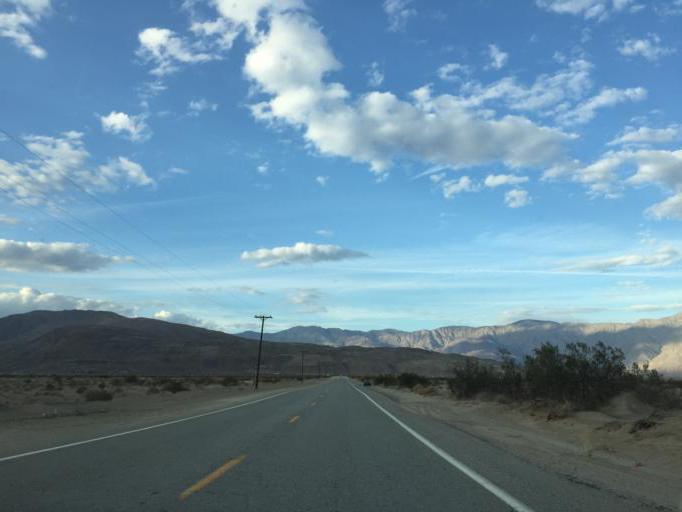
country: US
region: California
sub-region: San Diego County
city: Borrego Springs
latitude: 33.2789
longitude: -116.2986
